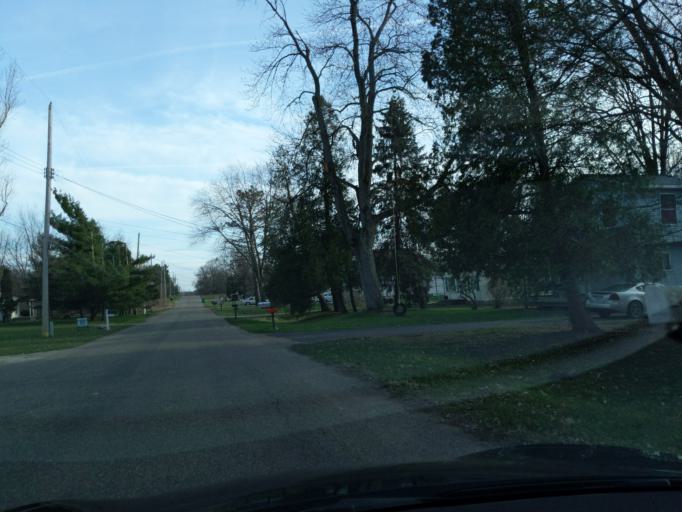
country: US
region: Michigan
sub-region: Eaton County
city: Waverly
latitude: 42.7185
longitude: -84.6190
